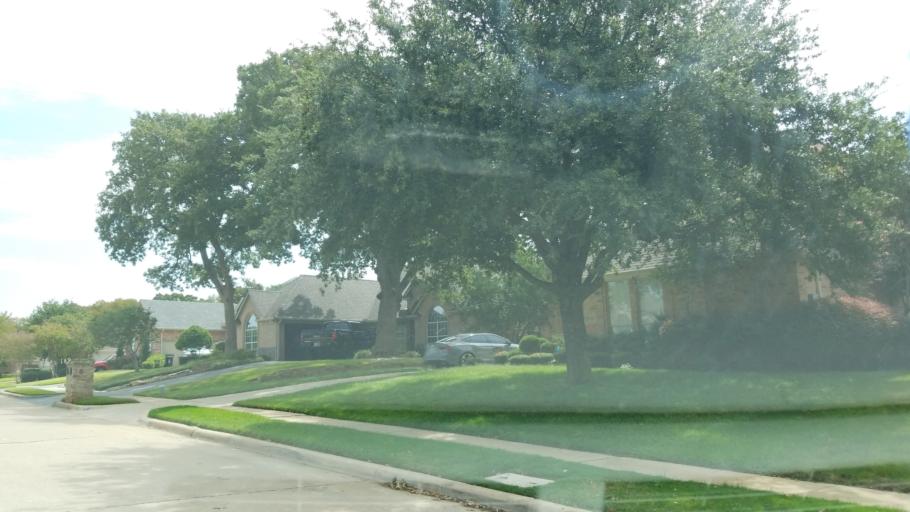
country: US
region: Texas
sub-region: Tarrant County
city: Grapevine
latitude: 32.8963
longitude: -97.1027
